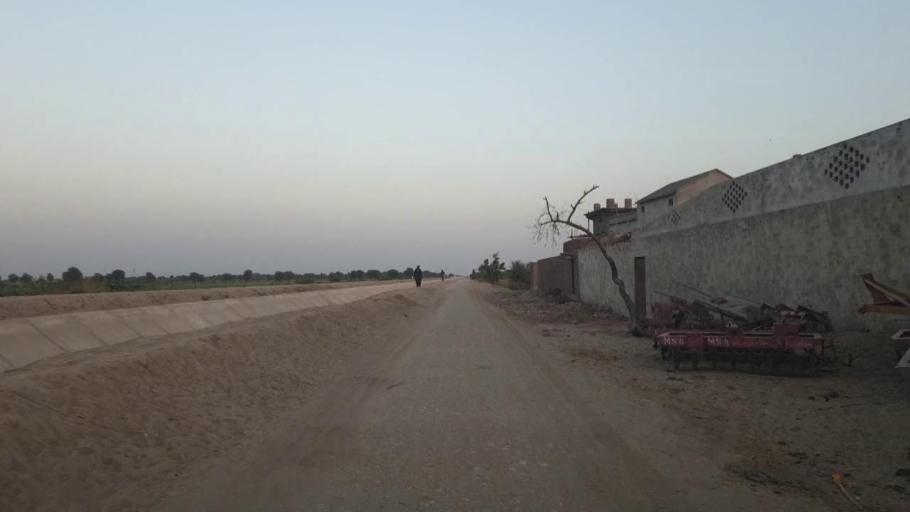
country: PK
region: Sindh
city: Umarkot
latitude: 25.4265
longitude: 69.6579
